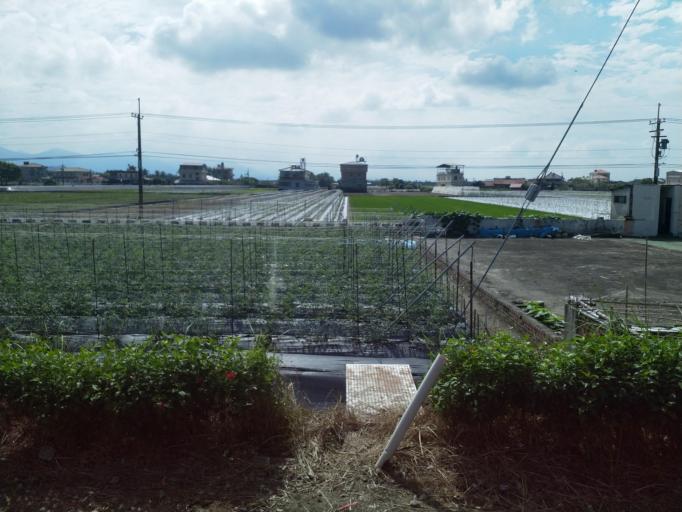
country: TW
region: Taiwan
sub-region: Pingtung
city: Pingtung
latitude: 22.8955
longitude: 120.5175
